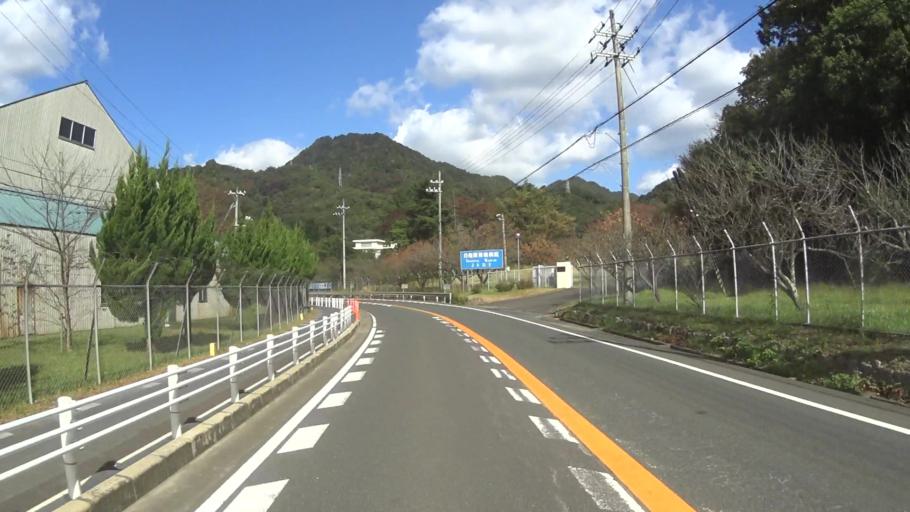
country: JP
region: Kyoto
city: Maizuru
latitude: 35.4790
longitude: 135.4004
